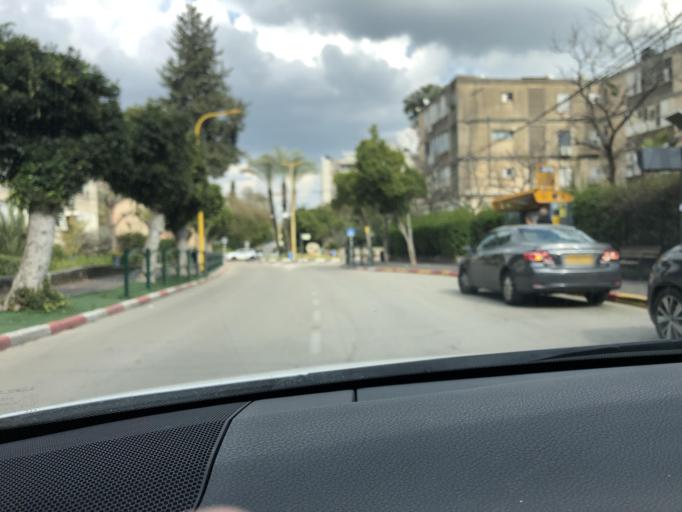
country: IL
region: Central District
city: Ganne Tiqwa
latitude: 32.0605
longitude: 34.8673
